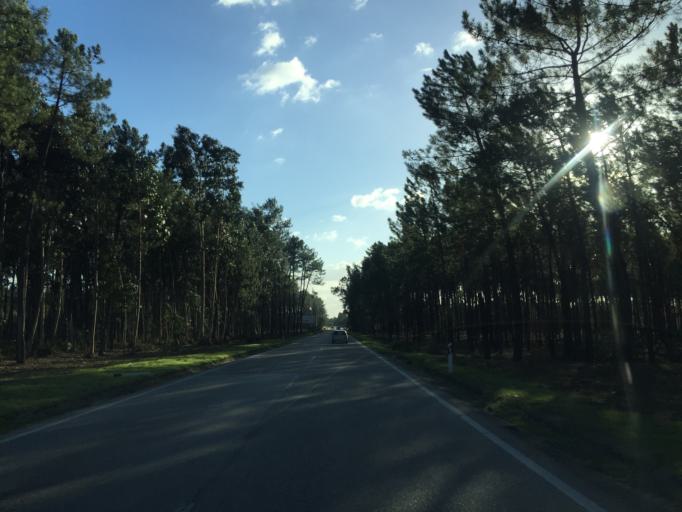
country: PT
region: Leiria
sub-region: Leiria
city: Monte Redondo
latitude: 39.9274
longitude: -8.8054
